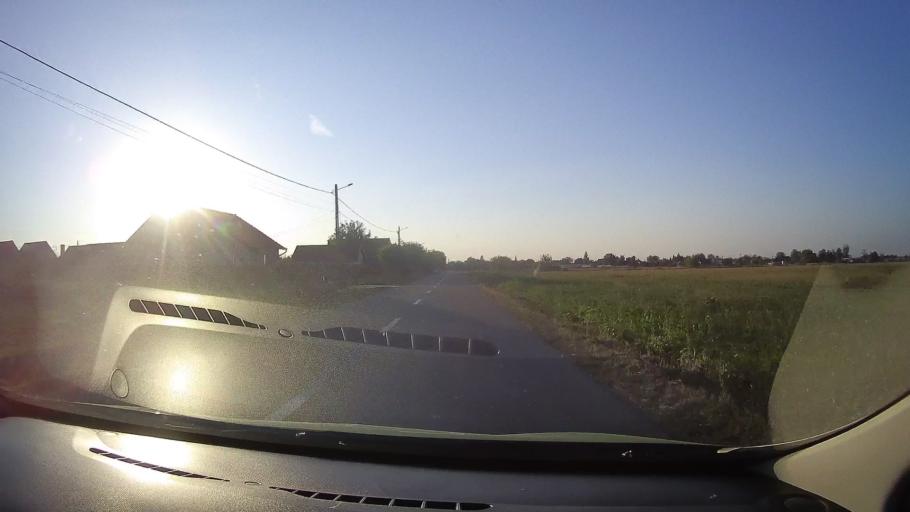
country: RO
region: Bihor
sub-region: Comuna Biharea
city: Biharea
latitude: 47.1637
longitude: 21.9536
